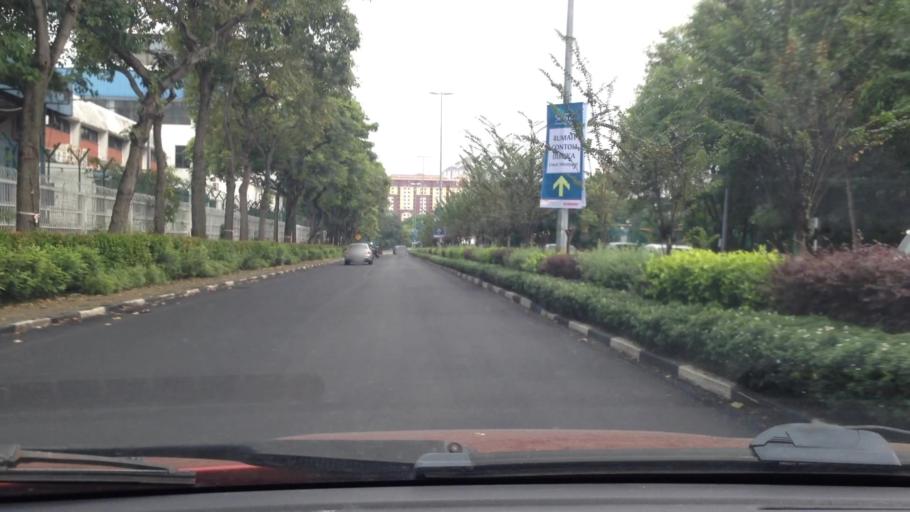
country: MY
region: Selangor
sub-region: Petaling
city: Petaling Jaya
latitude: 3.0896
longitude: 101.6070
